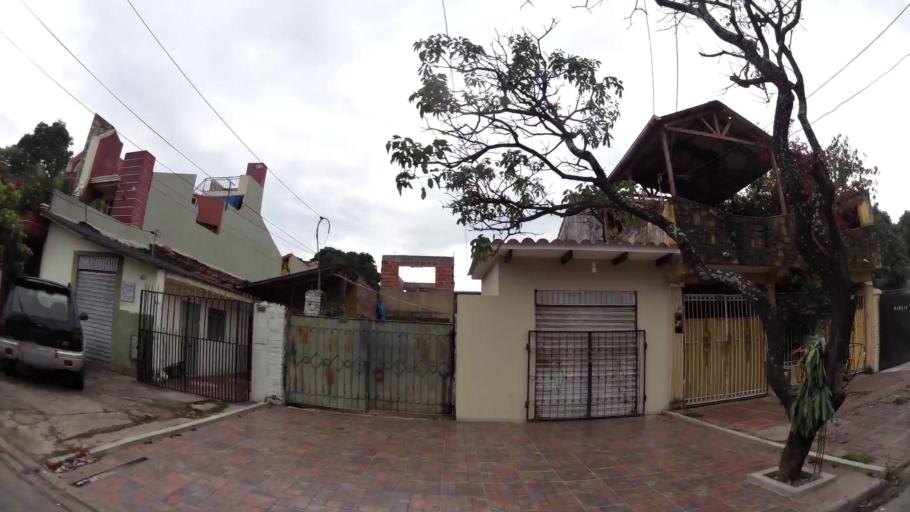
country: BO
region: Santa Cruz
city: Santa Cruz de la Sierra
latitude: -17.7808
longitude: -63.1611
